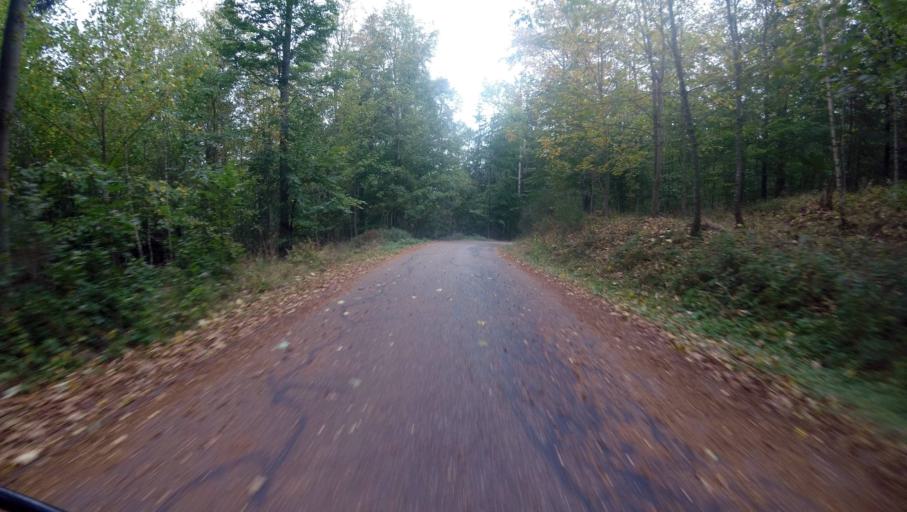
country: DE
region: Baden-Wuerttemberg
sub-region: Karlsruhe Region
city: Loffenau
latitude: 48.7717
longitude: 8.4166
